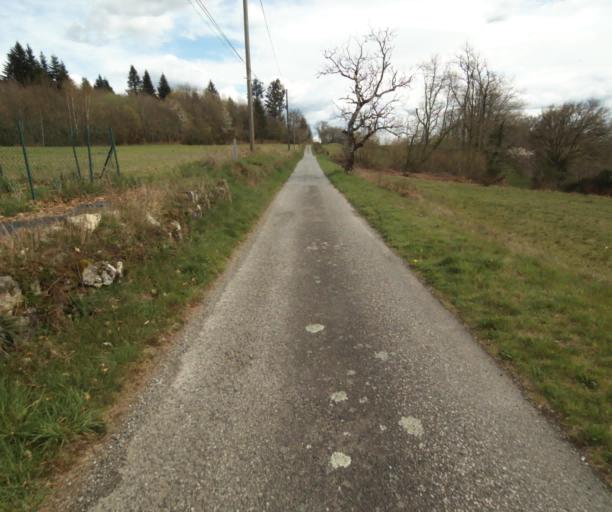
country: FR
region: Limousin
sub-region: Departement de la Correze
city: Argentat
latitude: 45.1935
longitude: 1.9492
